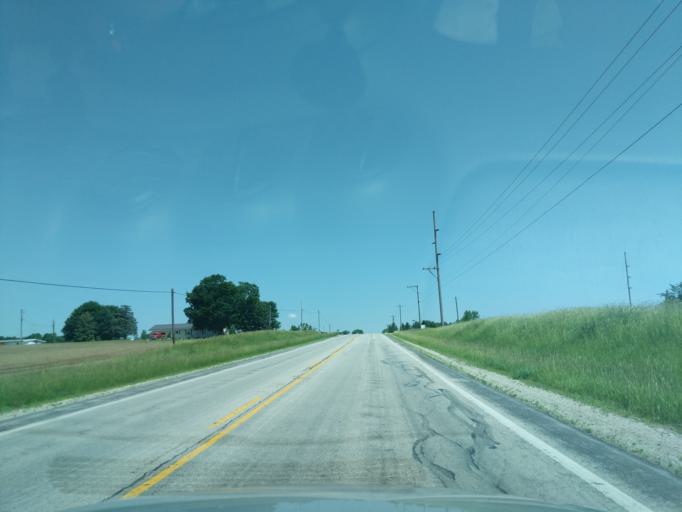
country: US
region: Indiana
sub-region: Whitley County
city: Columbia City
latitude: 41.2059
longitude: -85.4917
